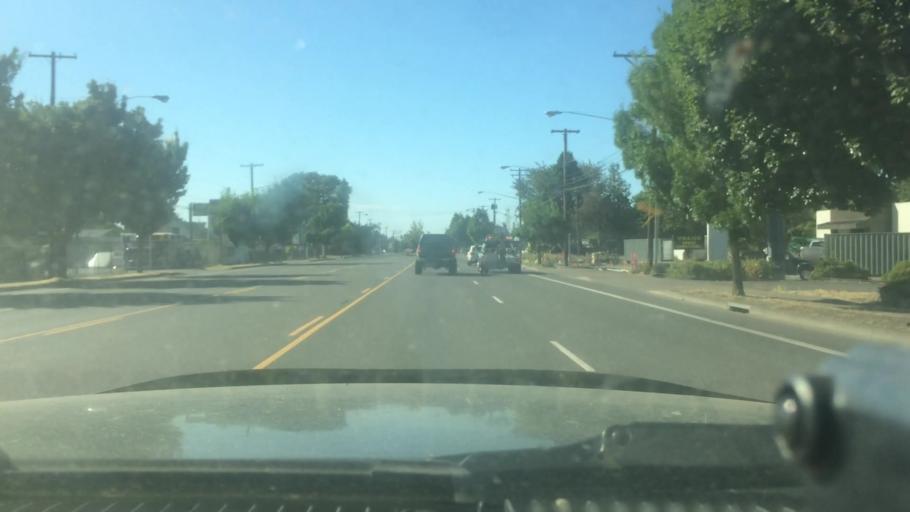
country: US
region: Oregon
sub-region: Lane County
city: Eugene
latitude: 44.0677
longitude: -123.1405
